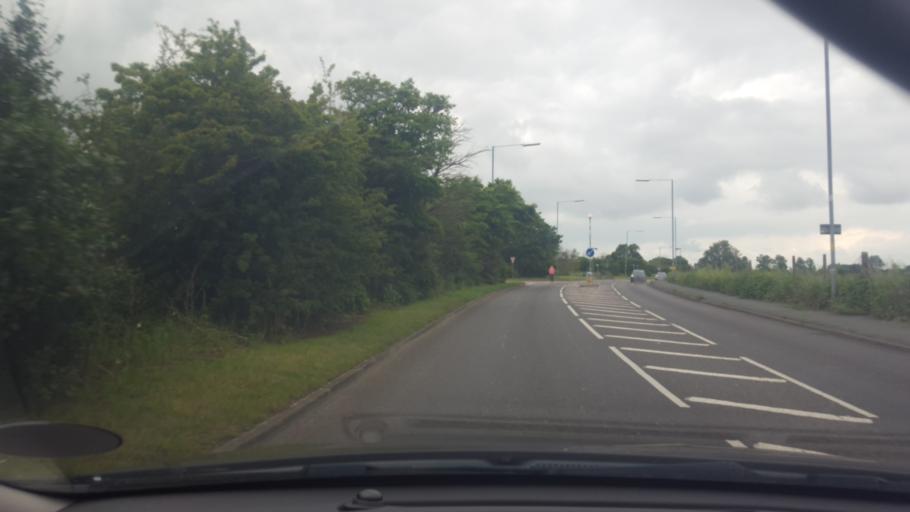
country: GB
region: England
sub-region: Essex
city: Clacton-on-Sea
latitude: 51.7942
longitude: 1.1198
